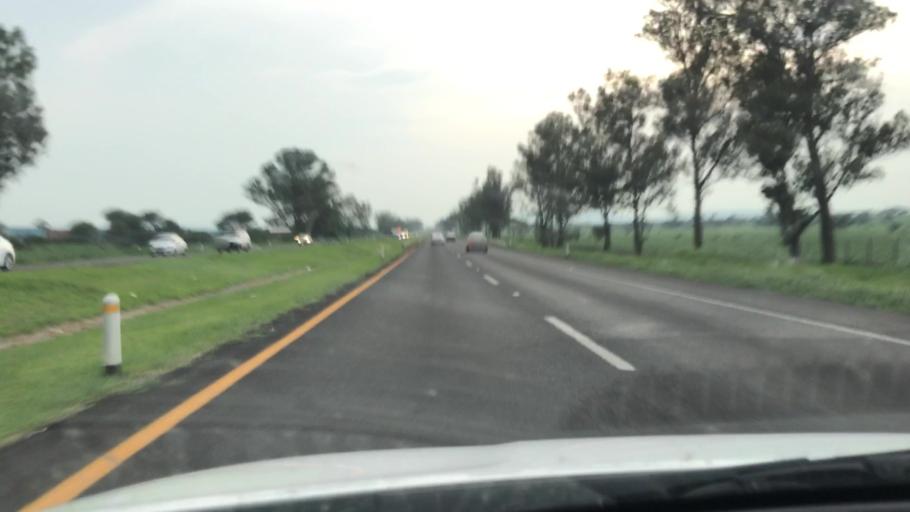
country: MX
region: Jalisco
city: Jamay
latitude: 20.3526
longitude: -102.6355
